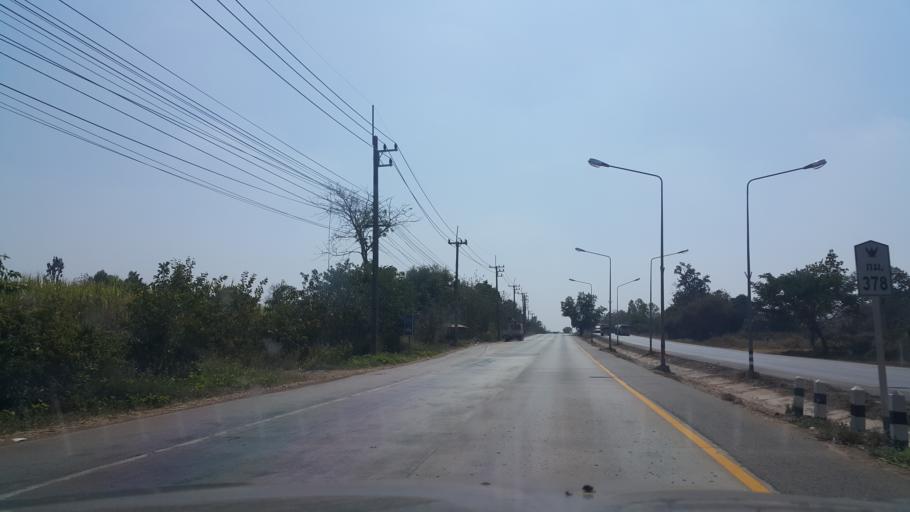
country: TH
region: Khon Kaen
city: Nam Phong
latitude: 16.7909
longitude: 102.8276
